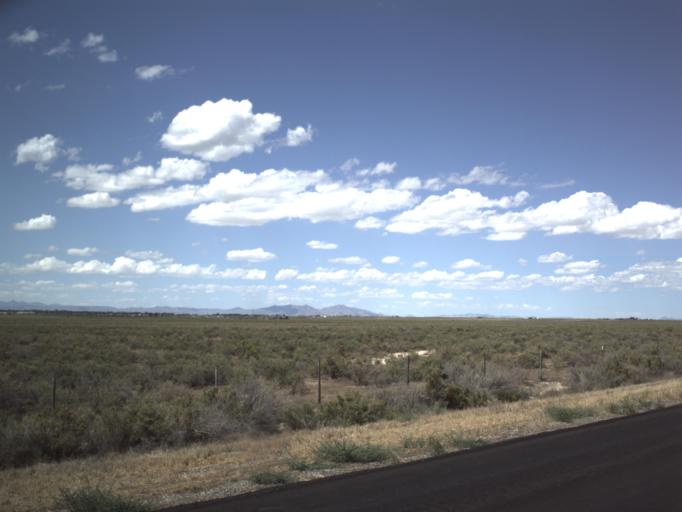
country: US
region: Utah
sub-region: Millard County
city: Delta
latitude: 39.3382
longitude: -112.4909
